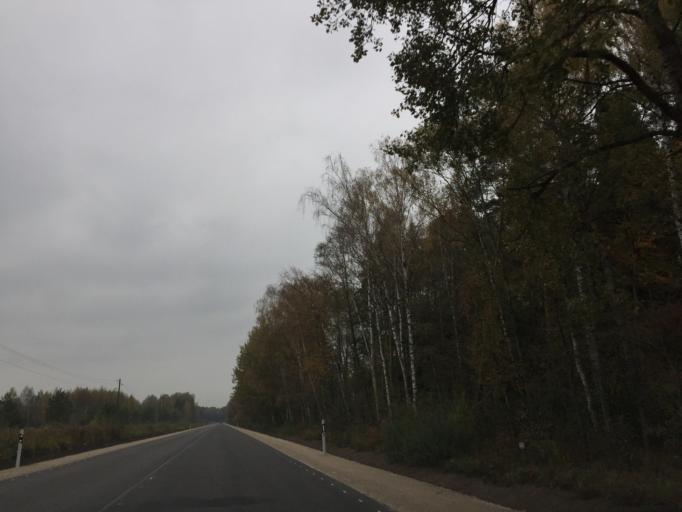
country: LV
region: Jelgava
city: Jelgava
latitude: 56.6546
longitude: 23.6143
